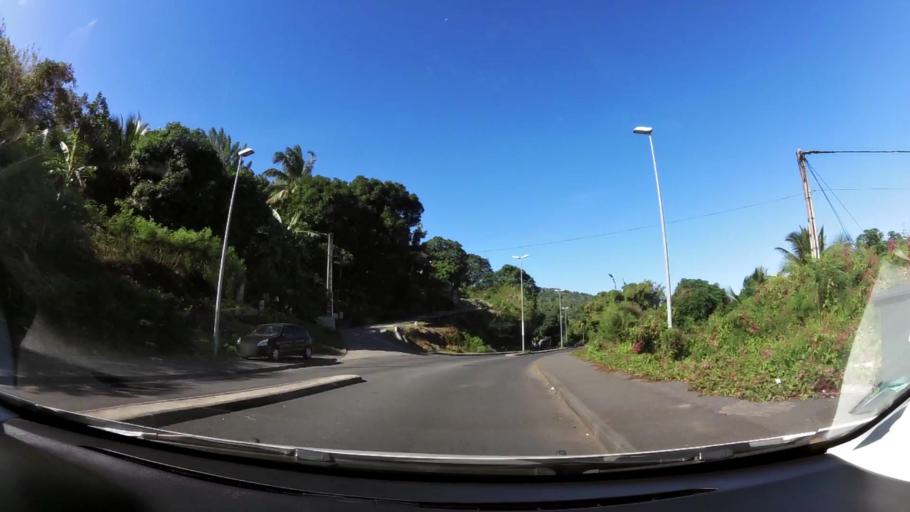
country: YT
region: Pamandzi
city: Pamandzi
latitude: -12.7940
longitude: 45.2755
